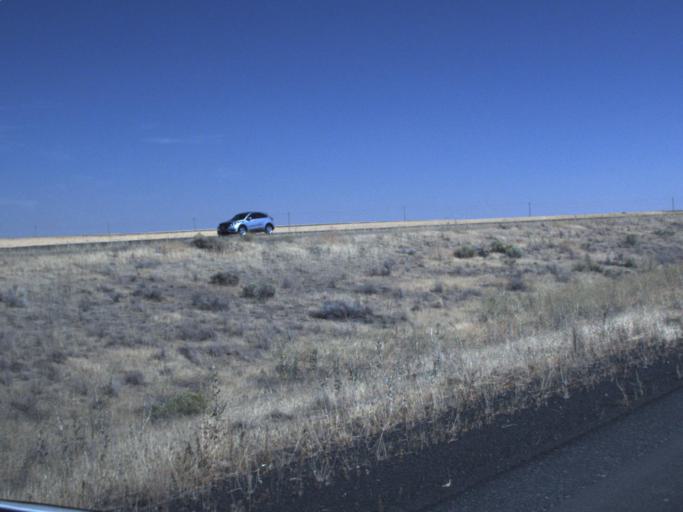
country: US
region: Washington
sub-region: Grant County
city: Warden
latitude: 47.0859
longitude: -118.8187
